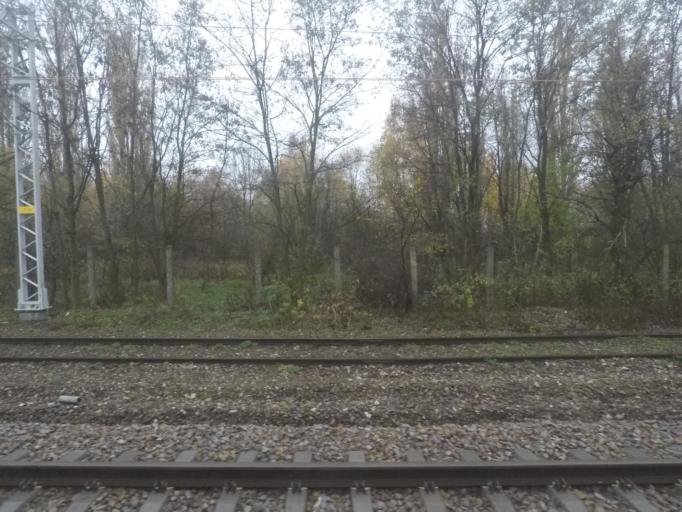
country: PL
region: Lesser Poland Voivodeship
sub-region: Powiat wielicki
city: Kokotow
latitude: 50.0914
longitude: 20.0821
